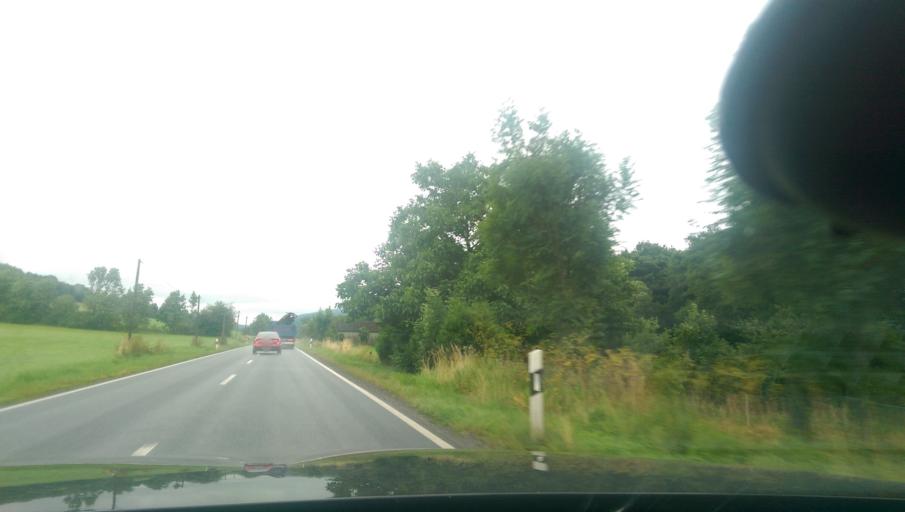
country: DE
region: Hesse
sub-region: Regierungsbezirk Kassel
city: Grossalmerode
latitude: 51.2353
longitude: 9.8126
